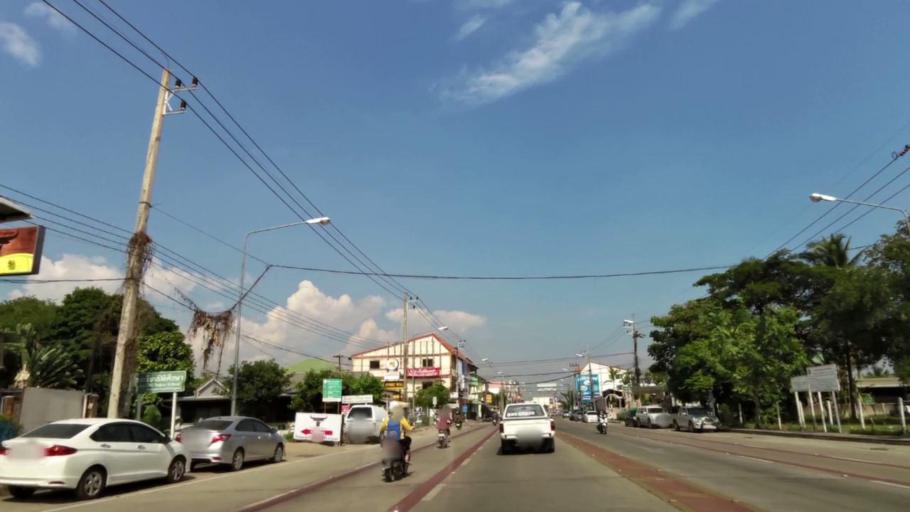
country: TH
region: Chiang Rai
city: Chiang Rai
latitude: 19.9215
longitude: 99.8337
